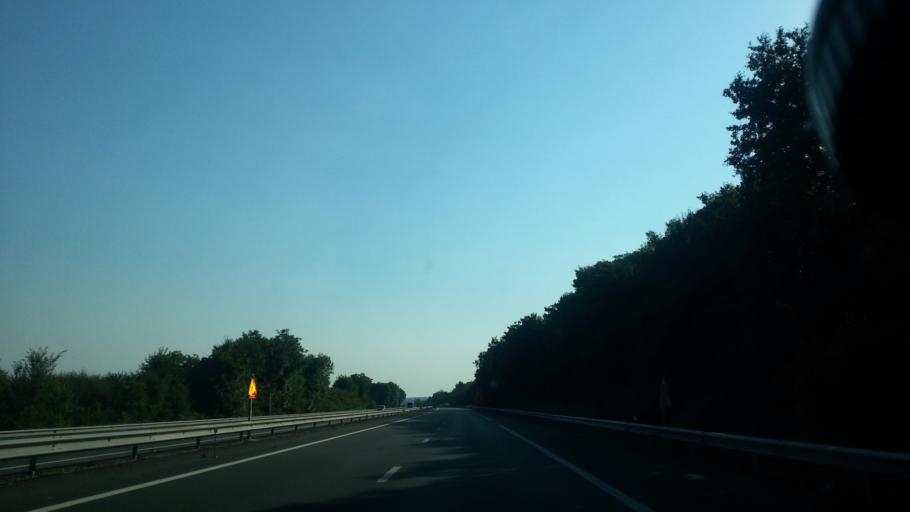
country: FR
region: Poitou-Charentes
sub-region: Departement de la Vienne
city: Rouille
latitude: 46.4585
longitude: 0.0045
